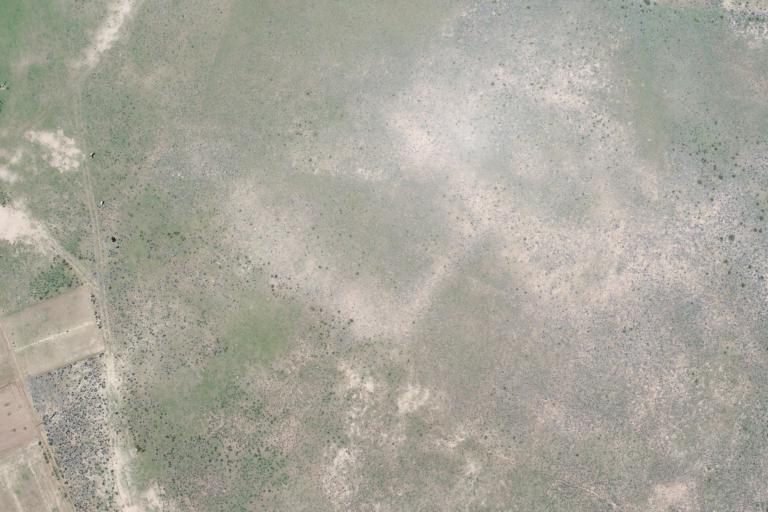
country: BO
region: La Paz
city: Curahuara de Carangas
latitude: -17.3112
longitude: -68.5149
